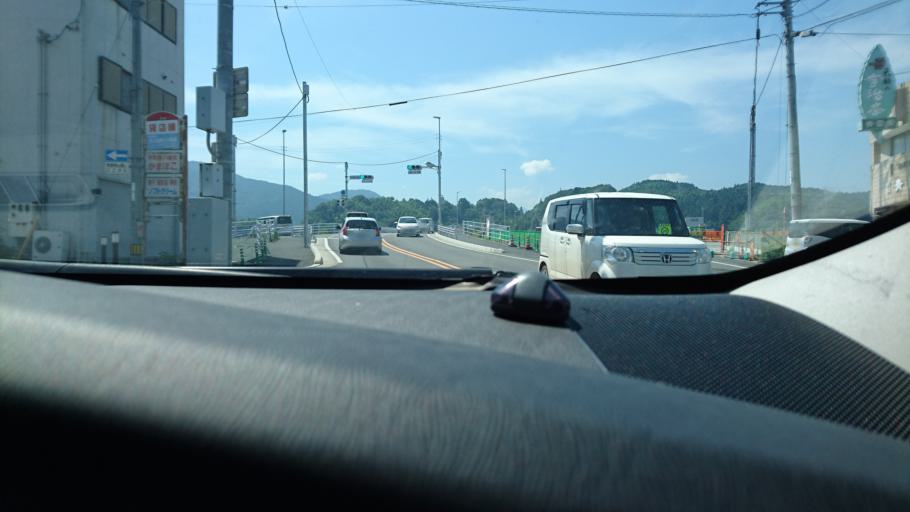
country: JP
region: Ehime
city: Ozu
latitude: 33.5102
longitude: 132.5455
